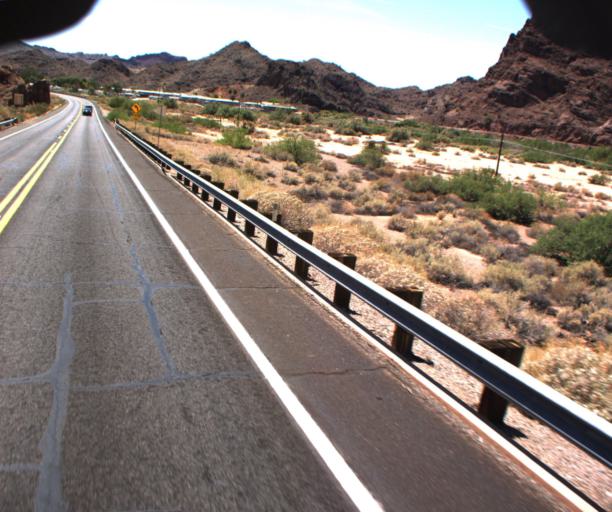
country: US
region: Arizona
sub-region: La Paz County
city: Cienega Springs
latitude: 34.2723
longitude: -114.1322
